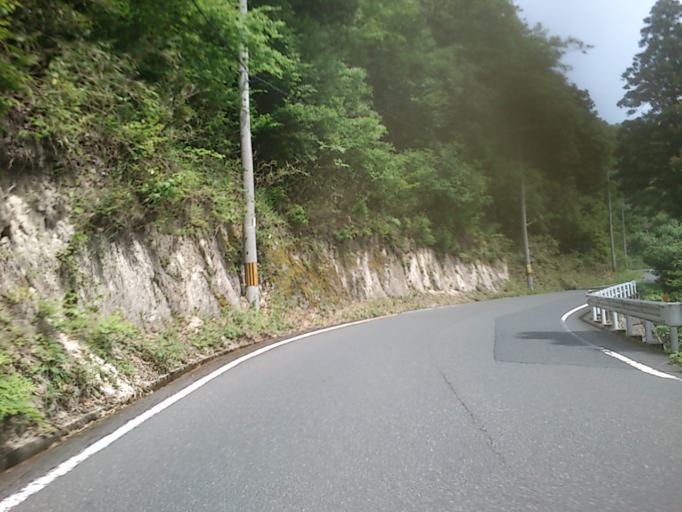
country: JP
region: Kyoto
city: Miyazu
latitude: 35.5885
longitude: 135.1170
